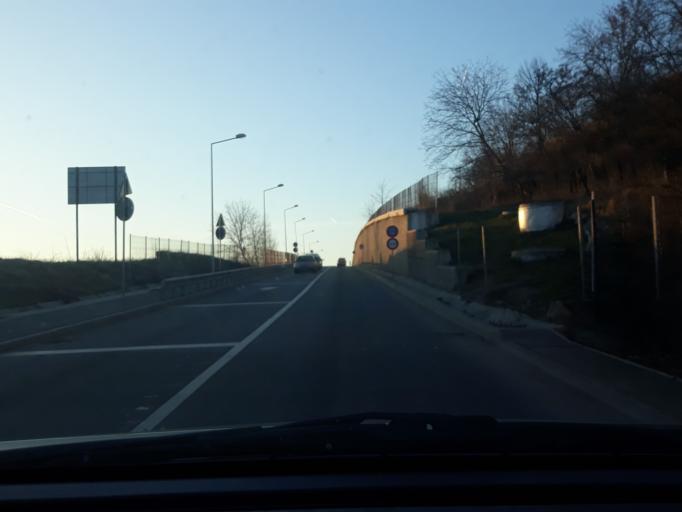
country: RO
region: Bihor
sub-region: Comuna Biharea
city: Oradea
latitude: 47.0533
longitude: 21.9554
